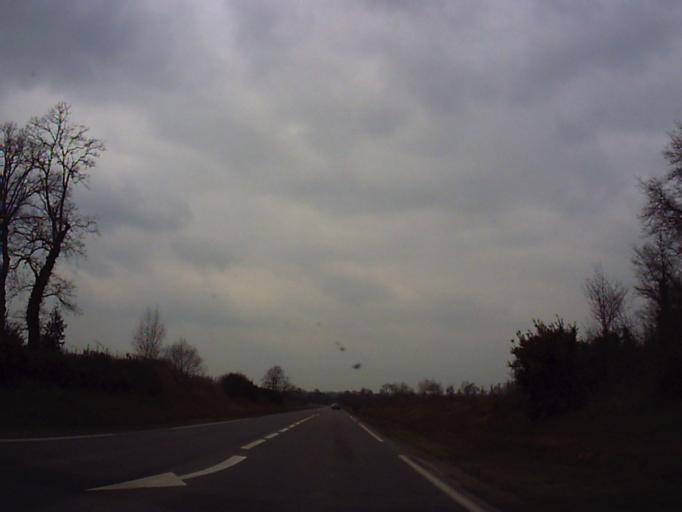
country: FR
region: Brittany
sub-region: Departement d'Ille-et-Vilaine
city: Le Rheu
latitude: 48.1250
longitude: -1.8005
